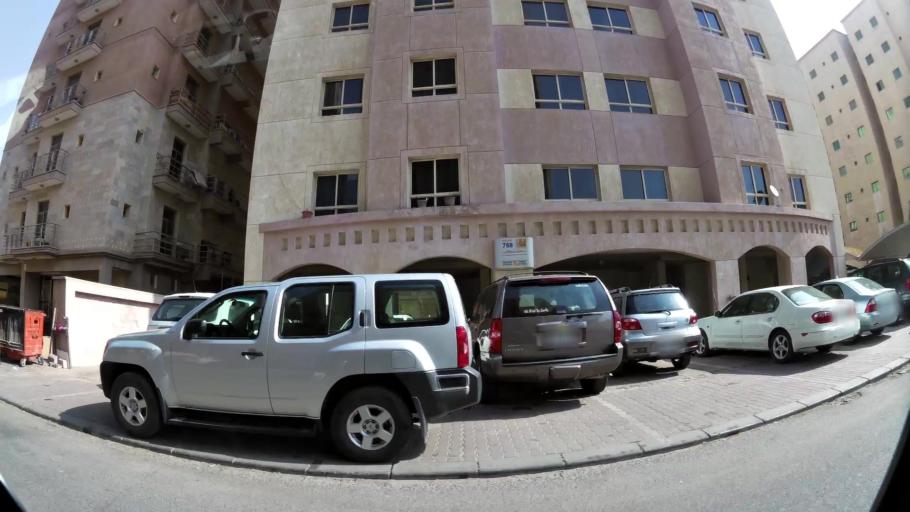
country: KW
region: Muhafazat Hawalli
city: Hawalli
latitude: 29.3377
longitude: 48.0310
